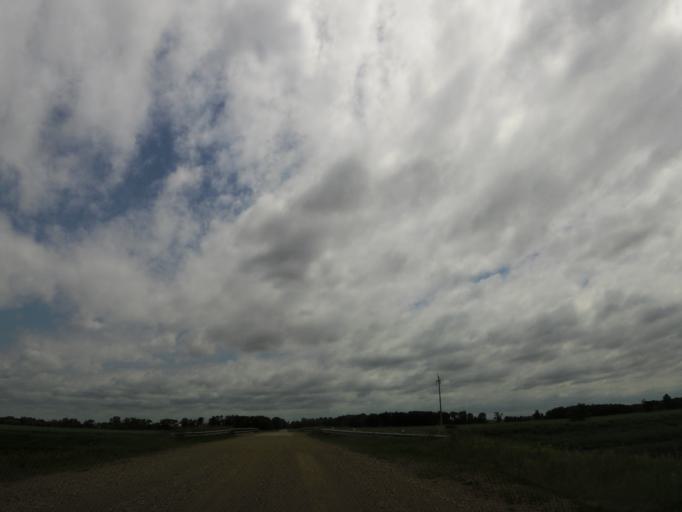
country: US
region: North Dakota
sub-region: Walsh County
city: Grafton
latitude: 48.4279
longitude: -97.4919
